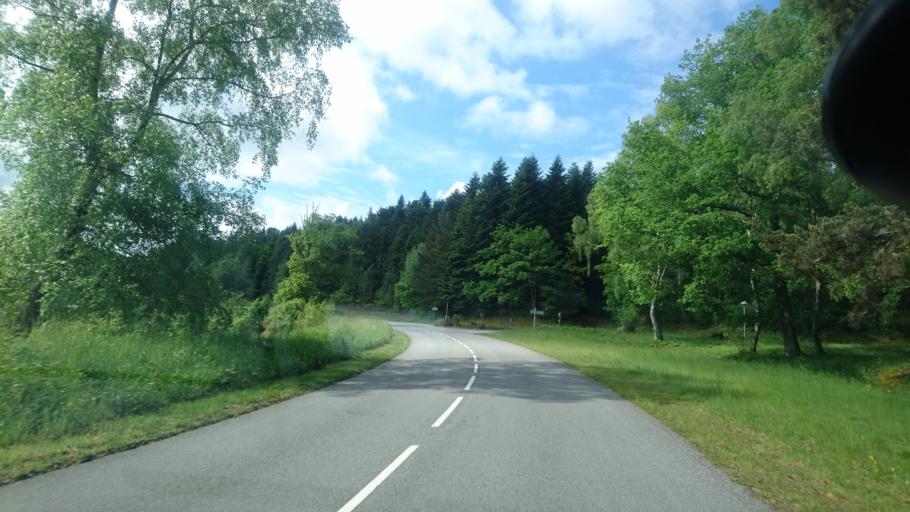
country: FR
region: Limousin
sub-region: Departement de la Haute-Vienne
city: Peyrat-le-Chateau
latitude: 45.8006
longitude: 1.8405
